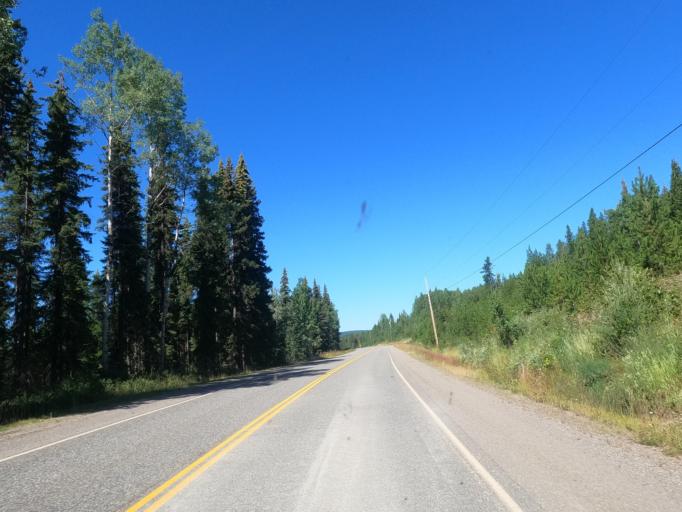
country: CA
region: British Columbia
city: Quesnel
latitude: 53.0306
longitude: -122.1089
